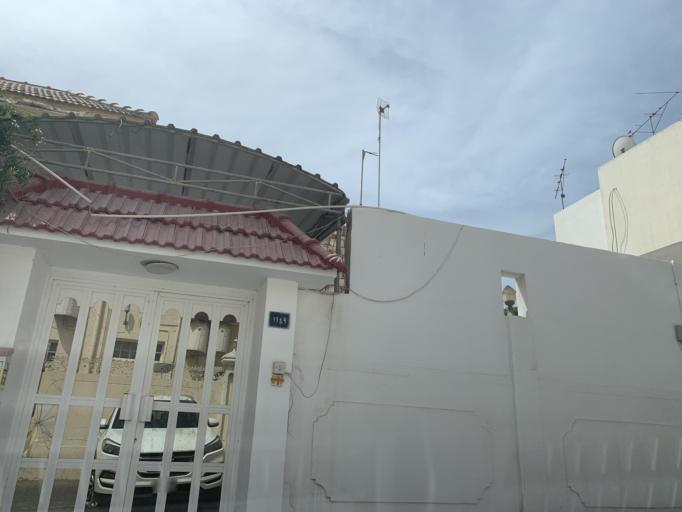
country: BH
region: Northern
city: Ar Rifa'
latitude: 26.1413
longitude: 50.5766
